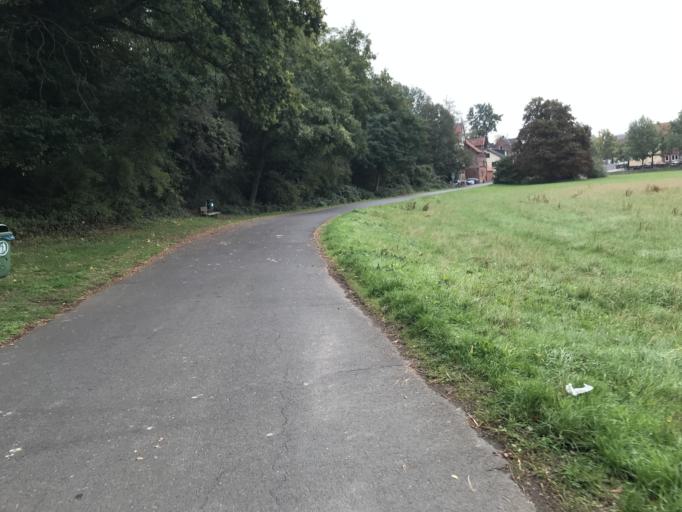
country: DE
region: Hesse
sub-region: Regierungsbezirk Kassel
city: Guxhagen
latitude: 51.2057
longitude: 9.4782
